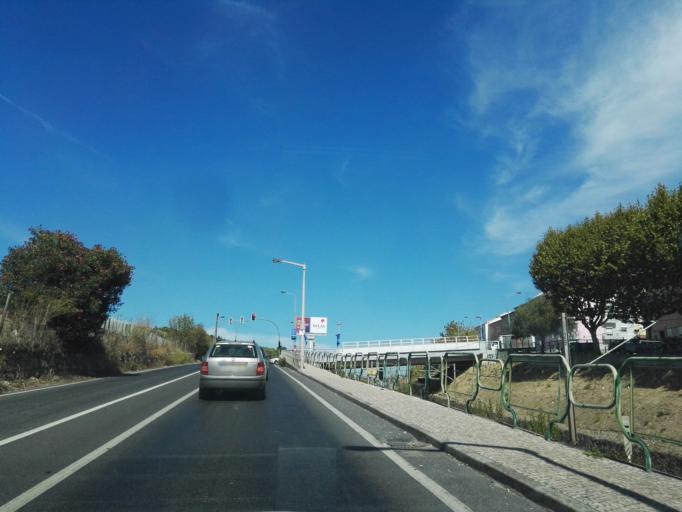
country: PT
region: Lisbon
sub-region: Vila Franca de Xira
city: Alhandra
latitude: 38.9296
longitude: -9.0098
